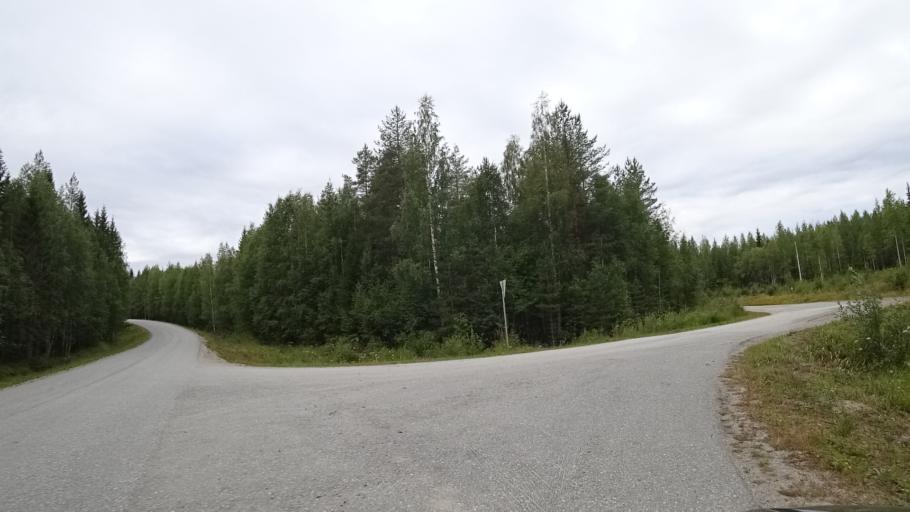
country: FI
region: North Karelia
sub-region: Joensuu
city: Ilomantsi
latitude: 63.1538
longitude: 30.6226
